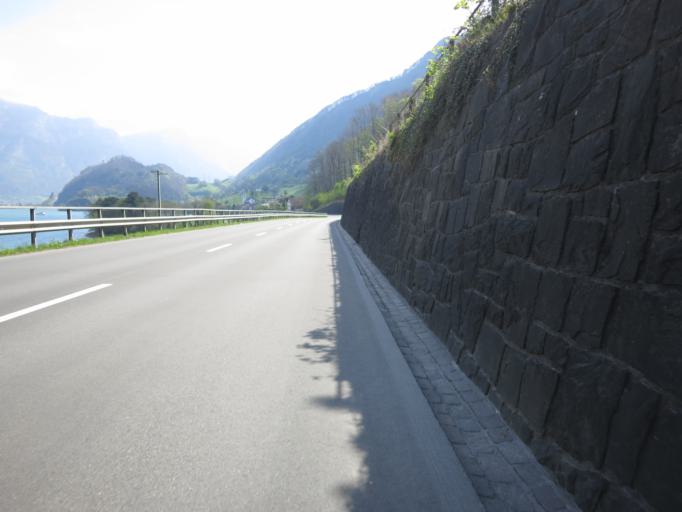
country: CH
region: Saint Gallen
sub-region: Wahlkreis Sarganserland
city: Quarten
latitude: 47.1147
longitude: 9.2686
